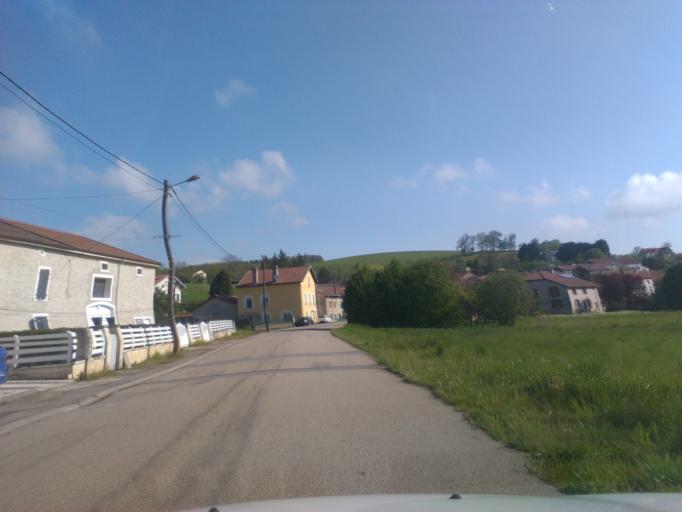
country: FR
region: Lorraine
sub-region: Departement des Vosges
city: Mirecourt
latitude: 48.3454
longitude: 6.1390
